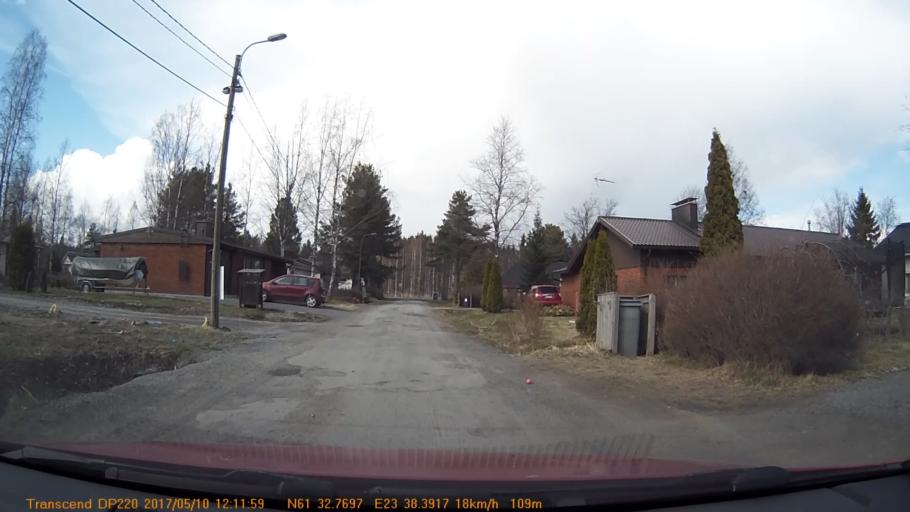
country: FI
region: Pirkanmaa
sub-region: Tampere
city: Yloejaervi
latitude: 61.5461
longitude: 23.6399
